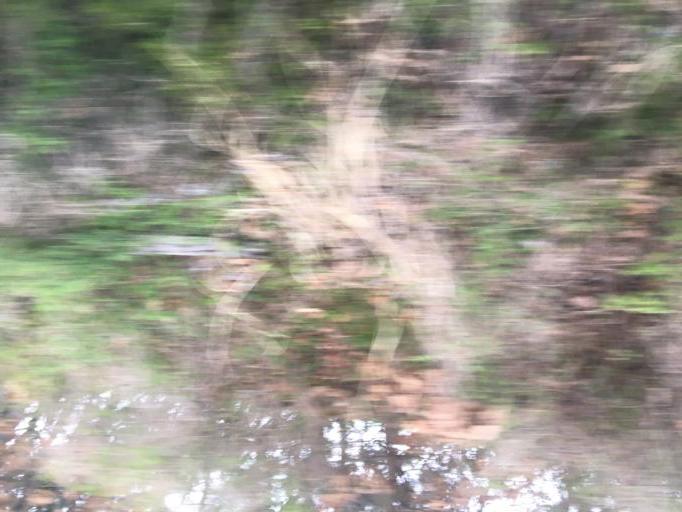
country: JP
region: Aomori
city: Shimokizukuri
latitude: 40.7638
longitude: 140.1644
